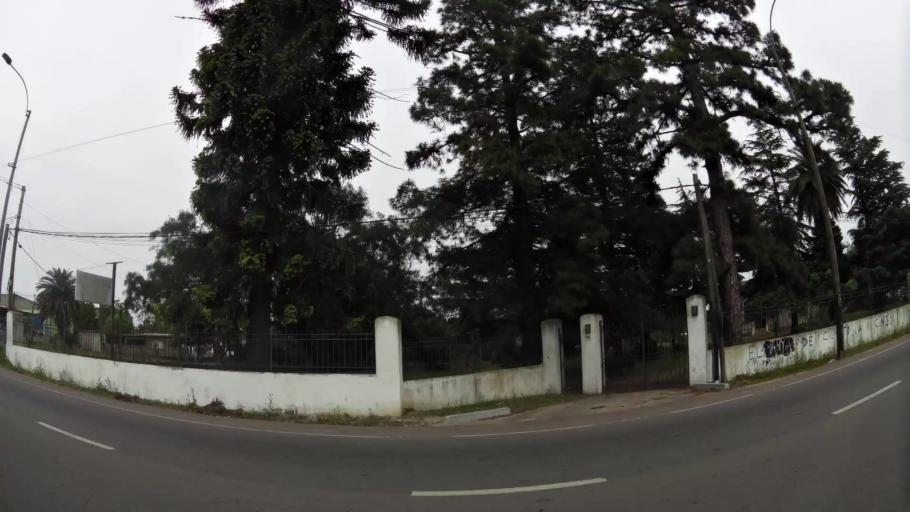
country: UY
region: Canelones
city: La Paz
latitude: -34.7712
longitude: -56.2270
